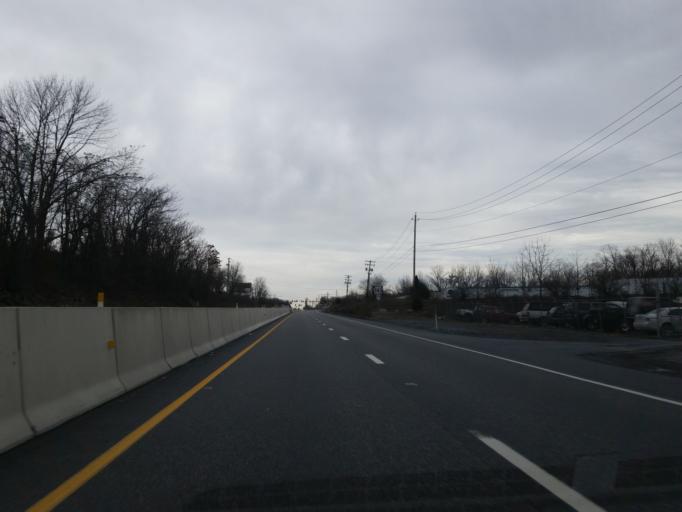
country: US
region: Pennsylvania
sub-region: Dauphin County
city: Skyline View
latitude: 40.3689
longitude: -76.6554
